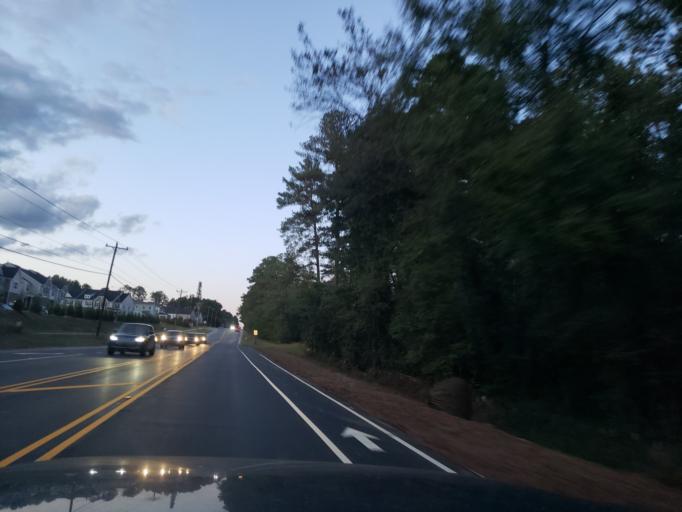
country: US
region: North Carolina
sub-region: Orange County
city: Chapel Hill
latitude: 35.8882
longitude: -78.9572
